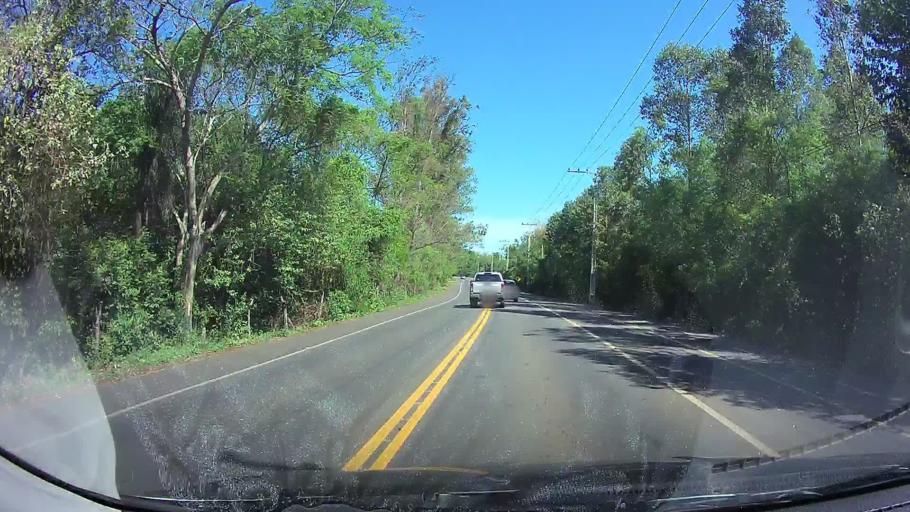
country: PY
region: Cordillera
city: San Bernardino
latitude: -25.2820
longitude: -57.3173
